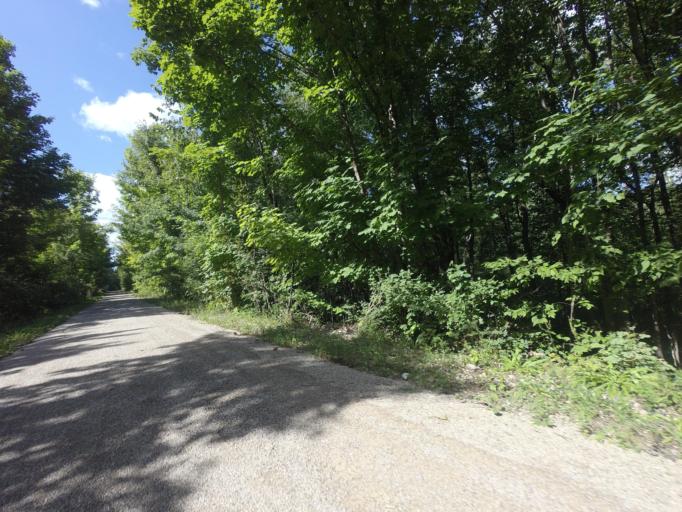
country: CA
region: Ontario
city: Huron East
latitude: 43.6740
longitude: -81.2843
